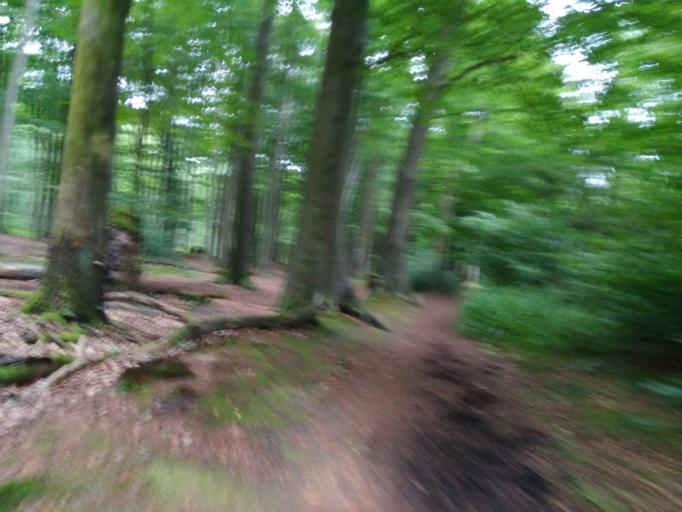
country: DE
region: North Rhine-Westphalia
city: Dorsten
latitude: 51.6217
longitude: 6.9900
